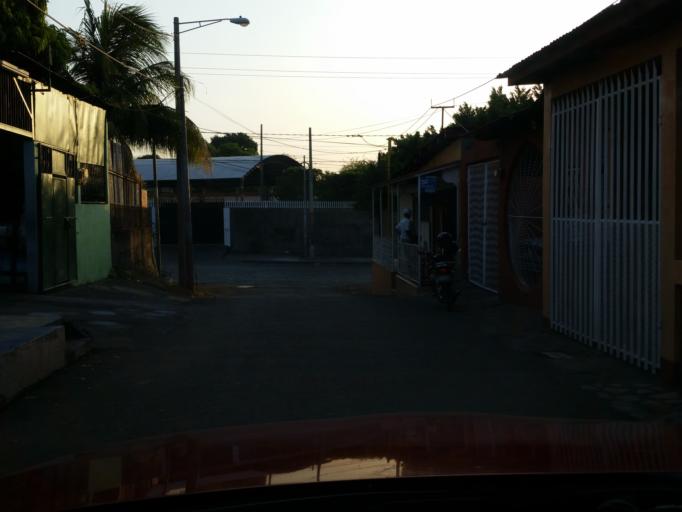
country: NI
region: Managua
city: Managua
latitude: 12.1373
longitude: -86.2584
